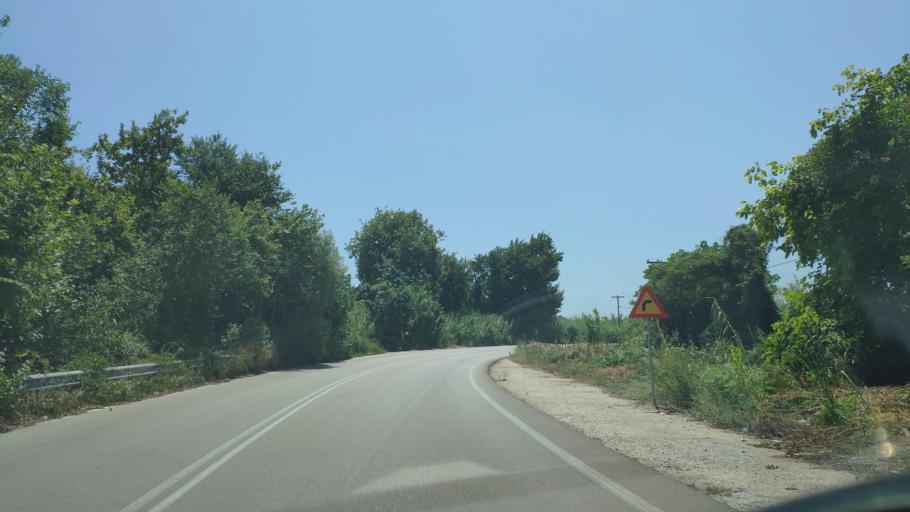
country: GR
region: Epirus
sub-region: Nomos Artas
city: Arta
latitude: 39.1485
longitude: 20.9770
